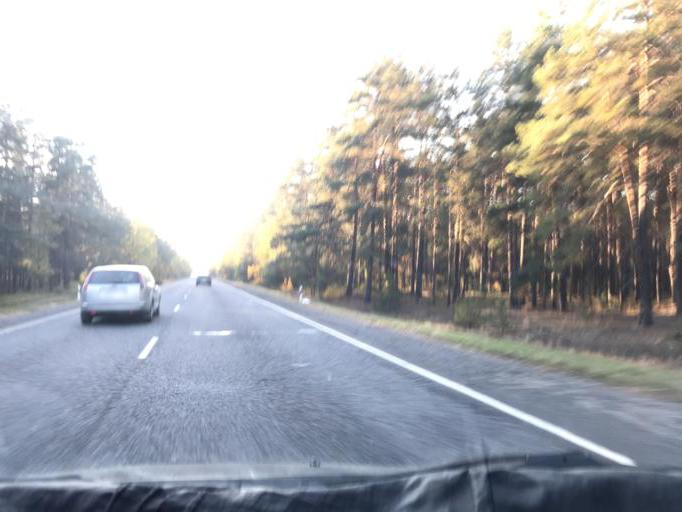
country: BY
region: Gomel
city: Zhytkavichy
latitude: 52.2727
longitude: 28.0433
